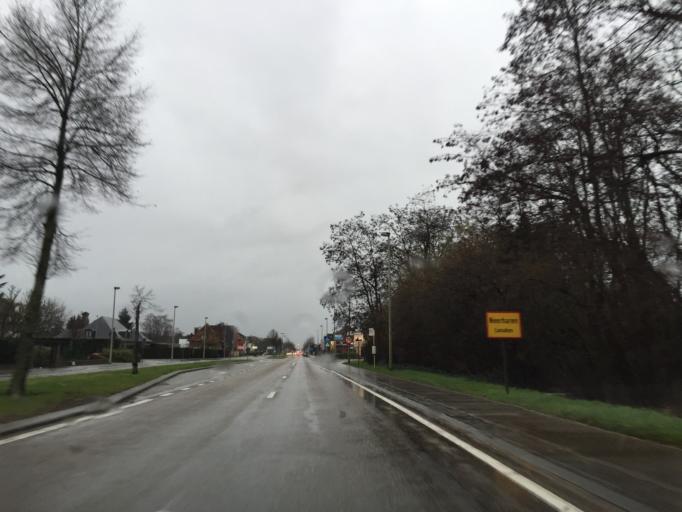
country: BE
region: Flanders
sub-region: Provincie Limburg
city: Lanaken
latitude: 50.9048
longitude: 5.6793
